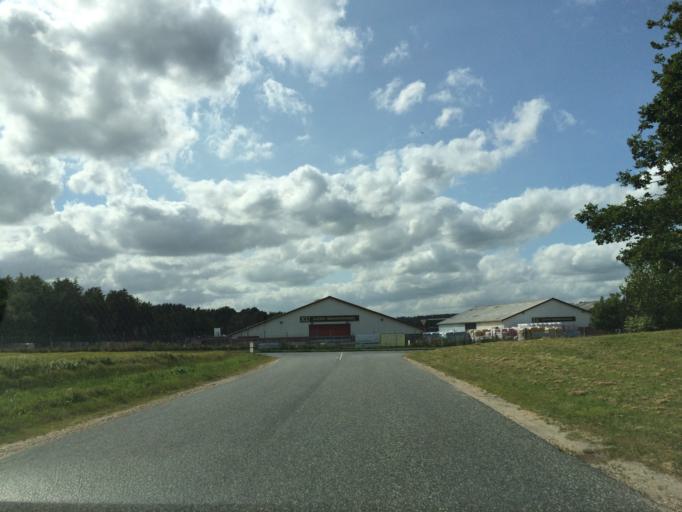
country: DK
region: Central Jutland
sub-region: Favrskov Kommune
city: Hammel
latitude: 56.2191
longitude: 9.7443
